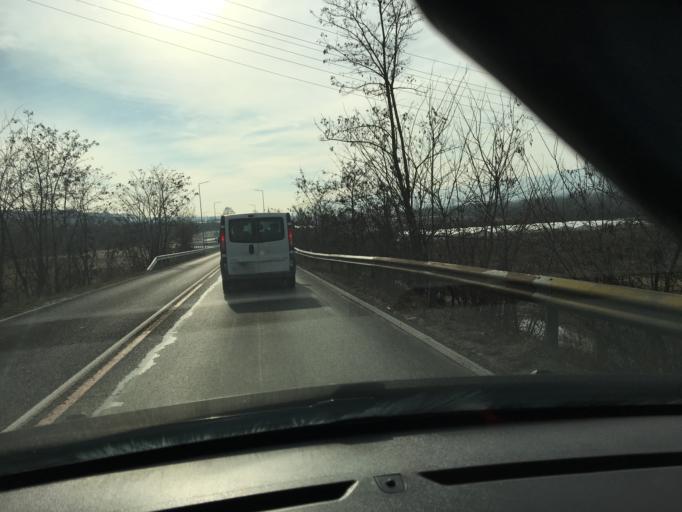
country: BG
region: Blagoevgrad
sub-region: Obshtina Kresna
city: Kresna
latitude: 41.7012
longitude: 23.1760
